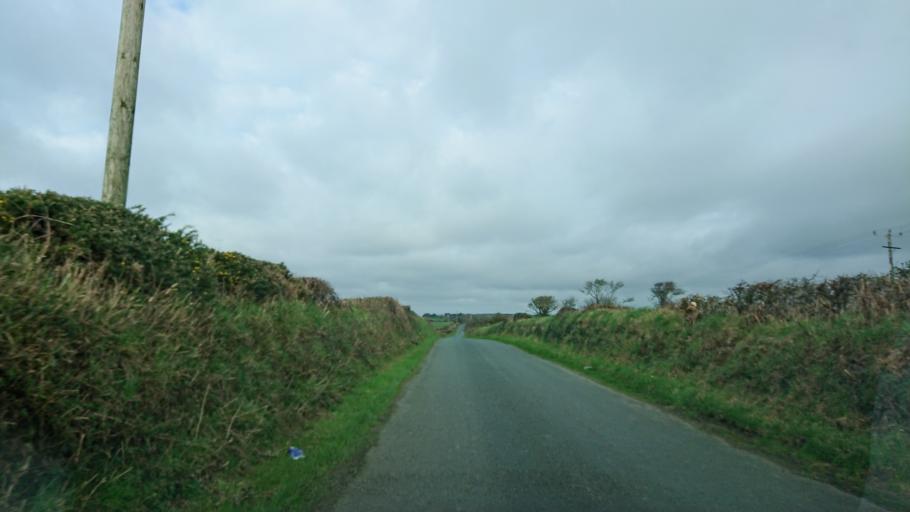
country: IE
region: Munster
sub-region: Waterford
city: Portlaw
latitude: 52.1529
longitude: -7.3099
